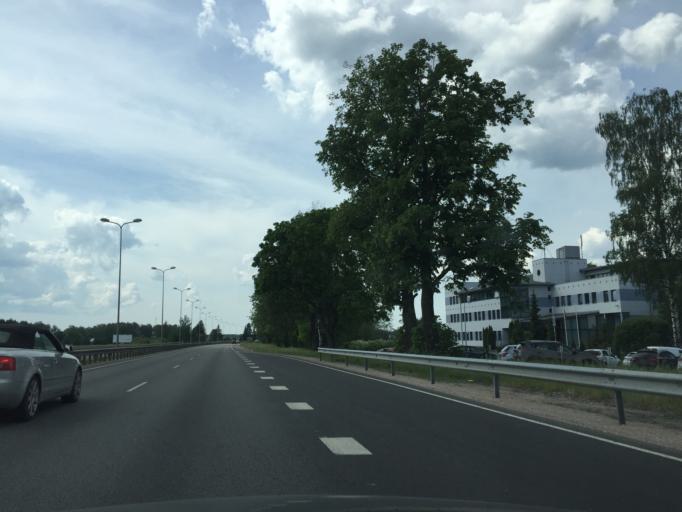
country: LV
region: Marupe
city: Marupe
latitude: 56.9265
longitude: 24.0020
